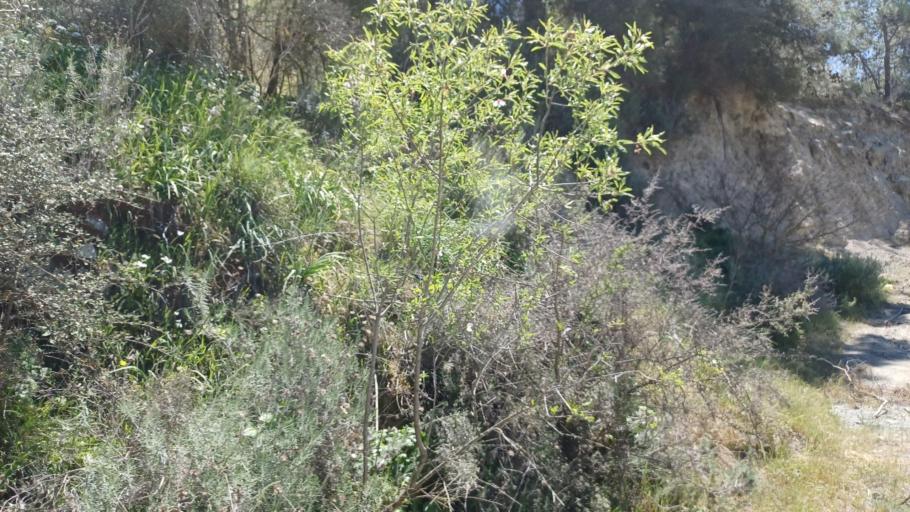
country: CY
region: Limassol
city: Parekklisha
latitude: 34.8161
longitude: 33.1462
